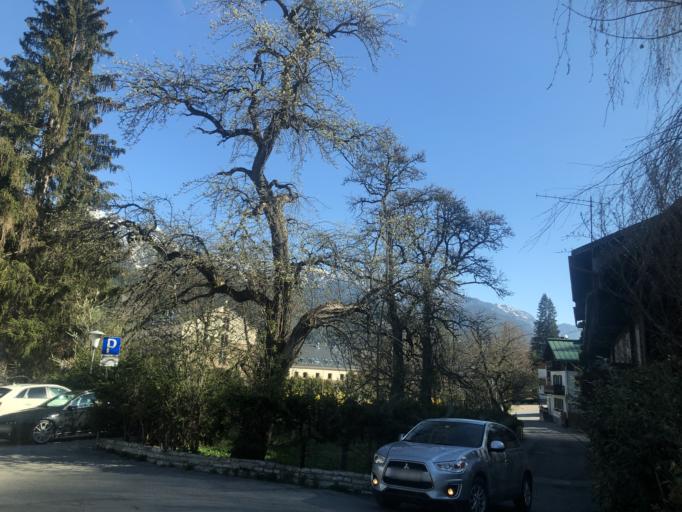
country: AT
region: Styria
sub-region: Politischer Bezirk Liezen
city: Schladming
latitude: 47.3907
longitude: 13.6906
